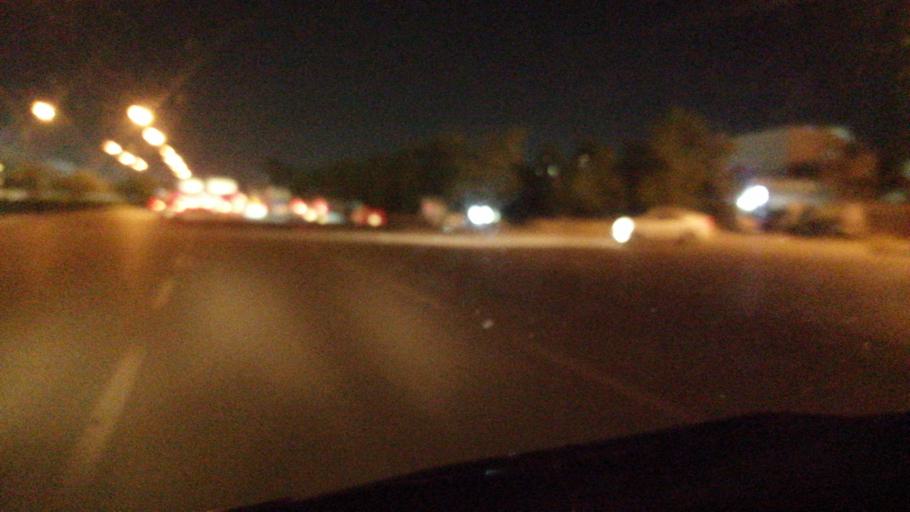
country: IQ
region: Arbil
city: Erbil
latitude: 36.1598
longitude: 43.9929
